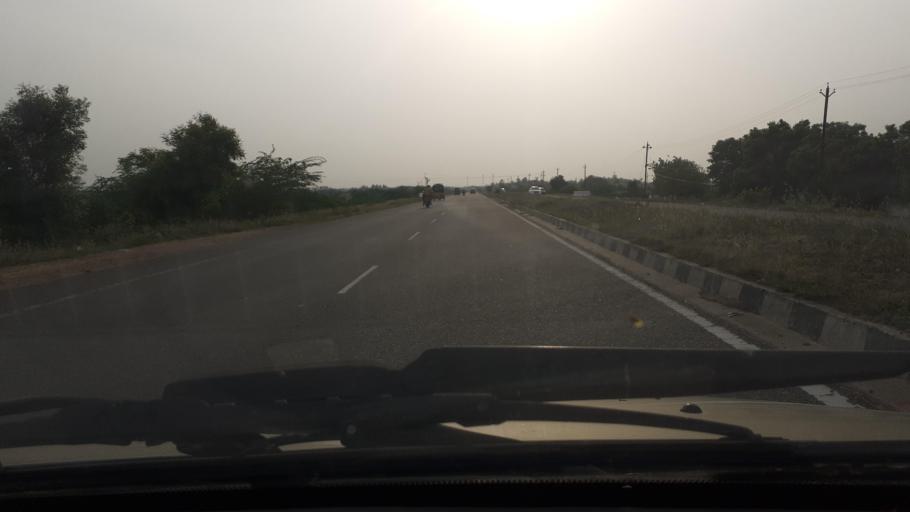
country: IN
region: Tamil Nadu
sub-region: Tirunelveli Kattabo
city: Tirunelveli
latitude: 8.7113
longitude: 77.8043
